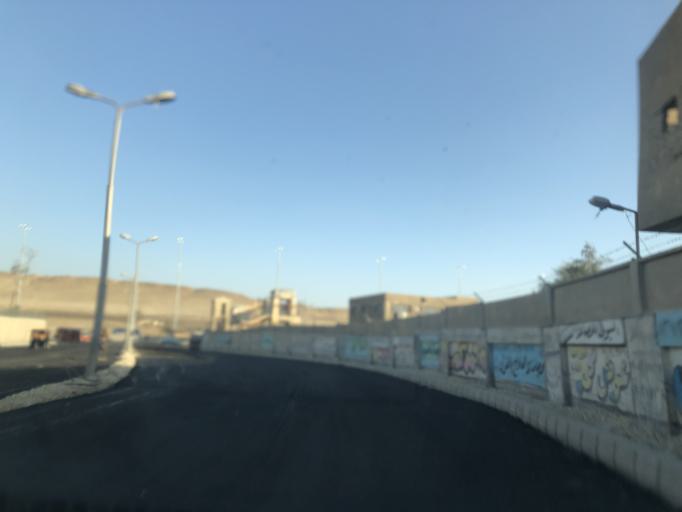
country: EG
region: Al Jizah
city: Al Jizah
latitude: 29.9797
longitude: 31.1129
